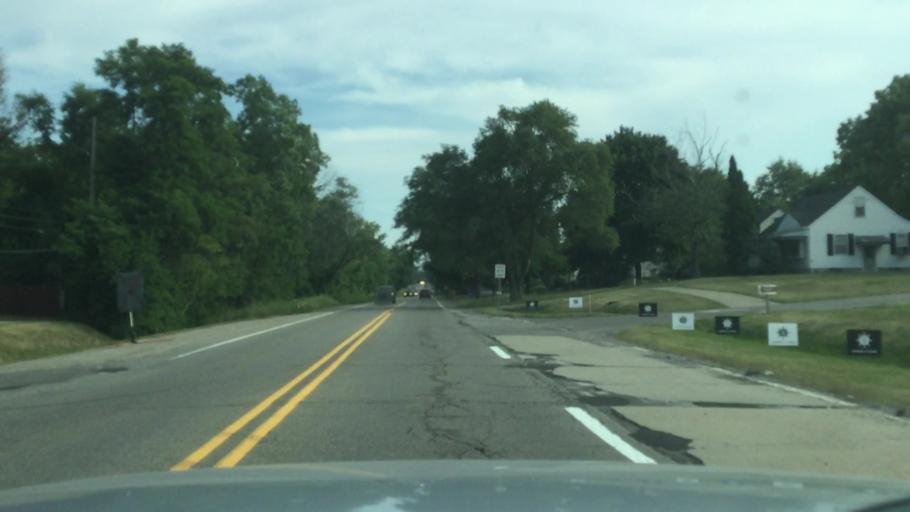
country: US
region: Michigan
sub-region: Oakland County
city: Keego Harbor
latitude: 42.6473
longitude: -83.3460
